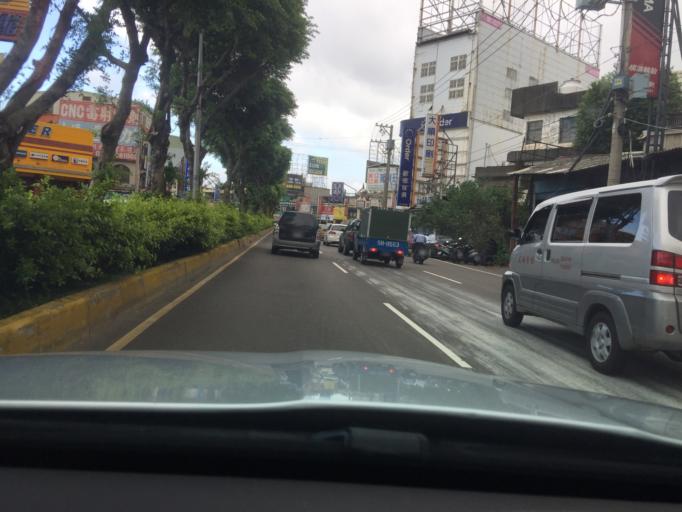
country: TW
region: Taiwan
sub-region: Hsinchu
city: Hsinchu
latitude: 24.8156
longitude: 120.9921
